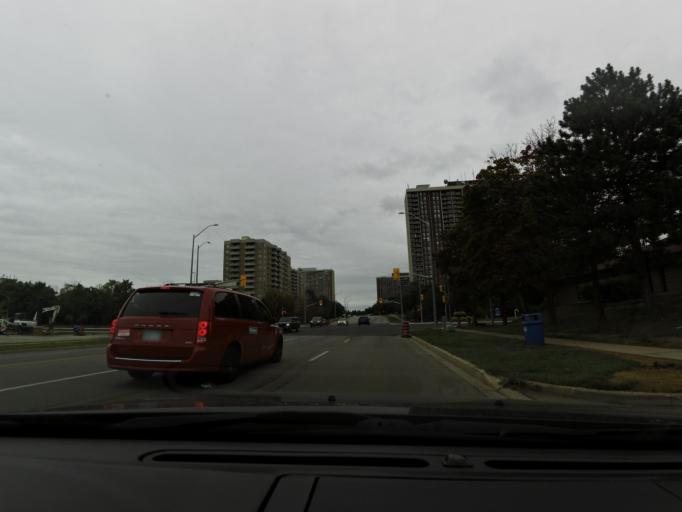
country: CA
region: Ontario
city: Brampton
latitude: 43.7174
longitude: -79.7179
